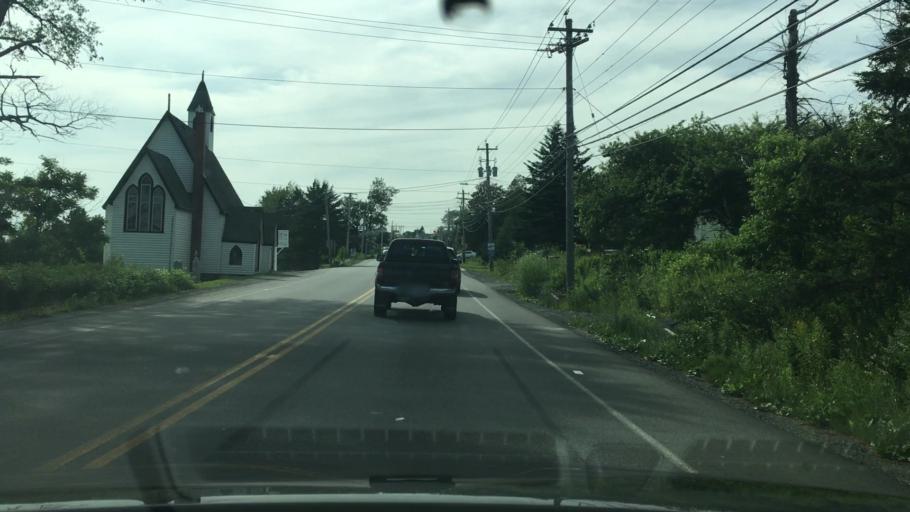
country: CA
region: Nova Scotia
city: Dartmouth
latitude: 44.7318
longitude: -63.7574
